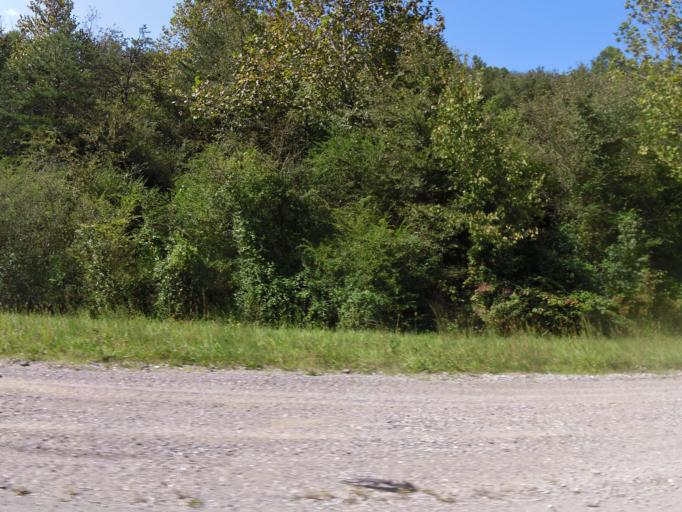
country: US
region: Kentucky
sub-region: Harlan County
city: Loyall
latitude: 36.8447
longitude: -83.4093
